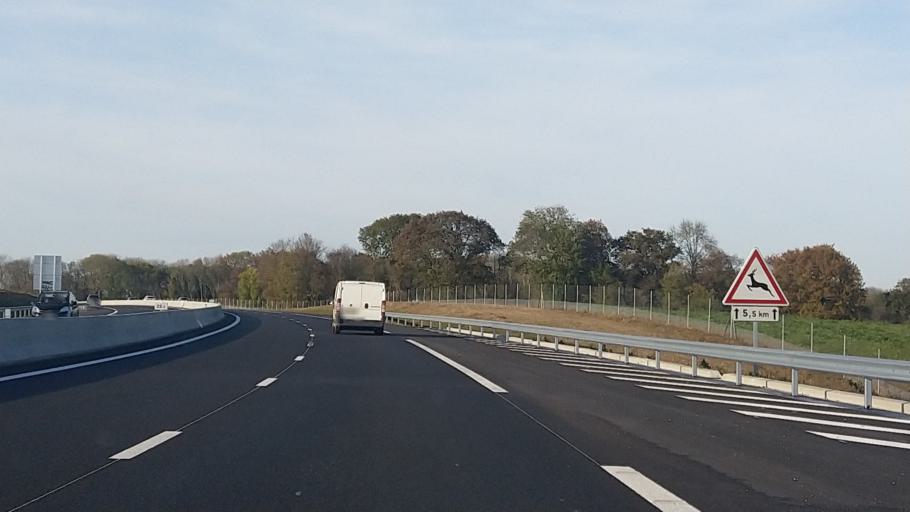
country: FR
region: Ile-de-France
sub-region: Departement du Val-d'Oise
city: Montsoult
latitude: 49.0785
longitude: 2.3316
